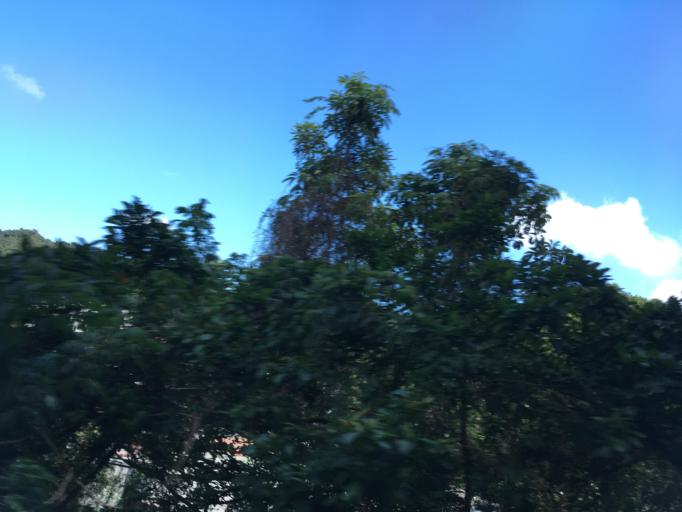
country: TW
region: Taipei
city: Taipei
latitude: 24.9495
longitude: 121.5543
